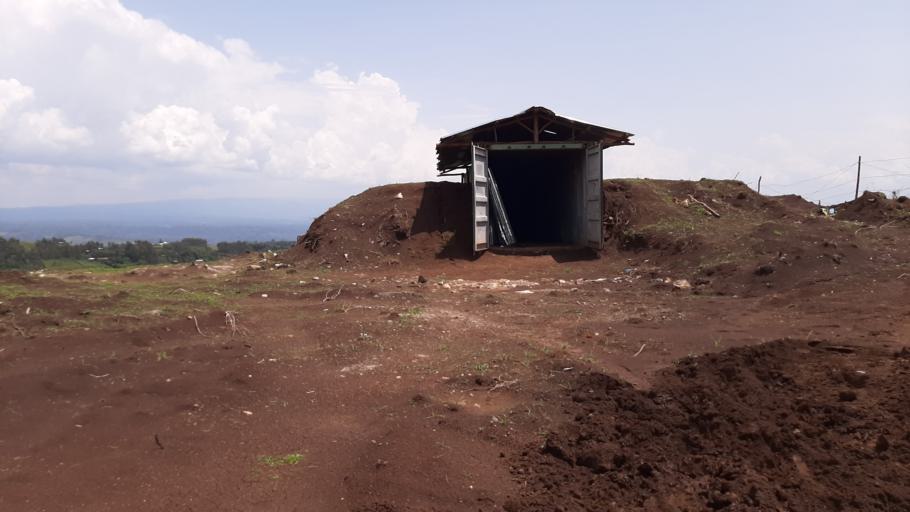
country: ET
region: Oromiya
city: Agaro
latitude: 7.9217
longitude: 36.7984
